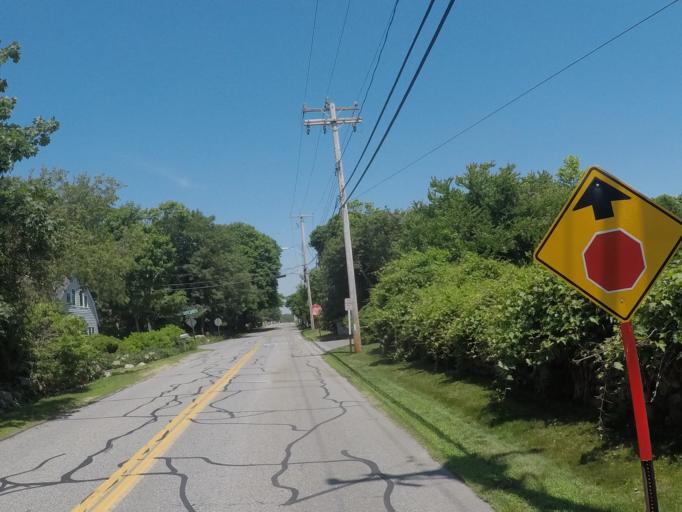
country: US
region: Massachusetts
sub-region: Bristol County
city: Bliss Corner
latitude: 41.5399
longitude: -70.9525
